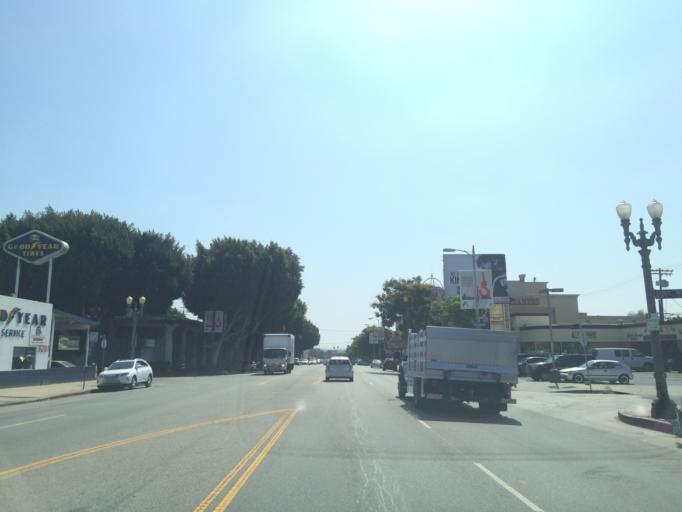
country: US
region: California
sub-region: Los Angeles County
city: Beverly Hills
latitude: 34.0553
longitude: -118.3924
